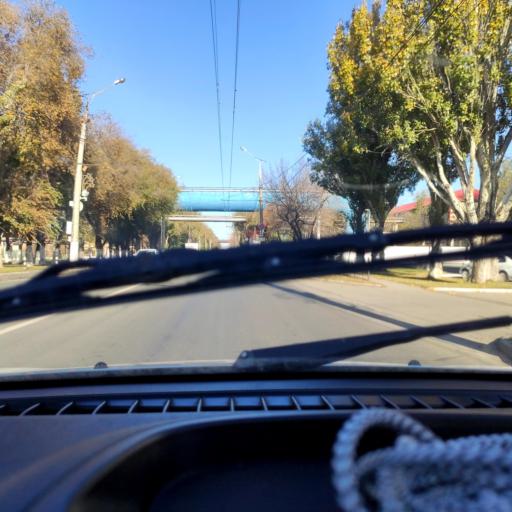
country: RU
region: Samara
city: Tol'yatti
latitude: 53.5555
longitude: 49.4514
